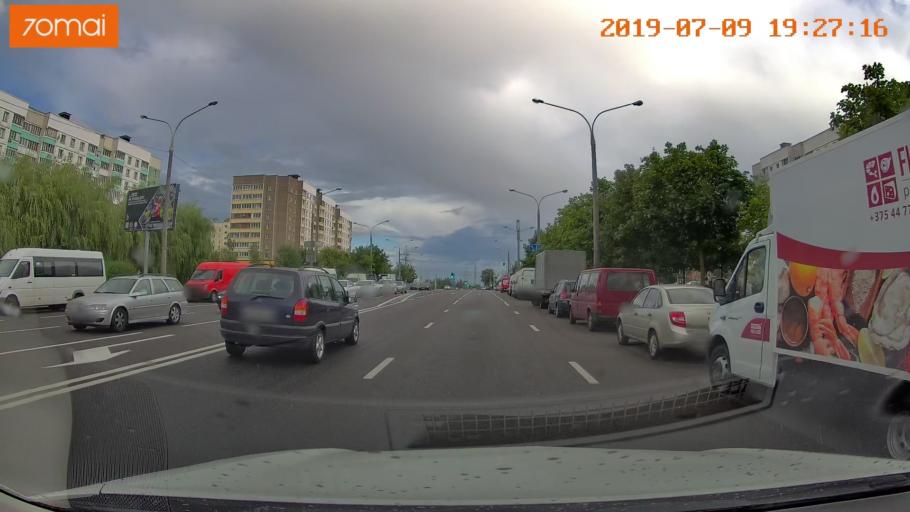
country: BY
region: Minsk
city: Syenitsa
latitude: 53.8382
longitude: 27.5744
